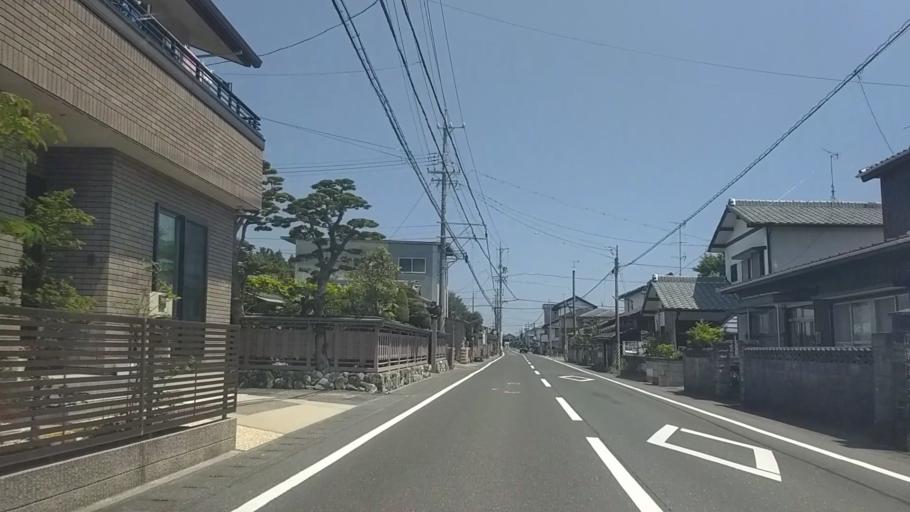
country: JP
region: Shizuoka
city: Hamamatsu
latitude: 34.6830
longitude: 137.6384
